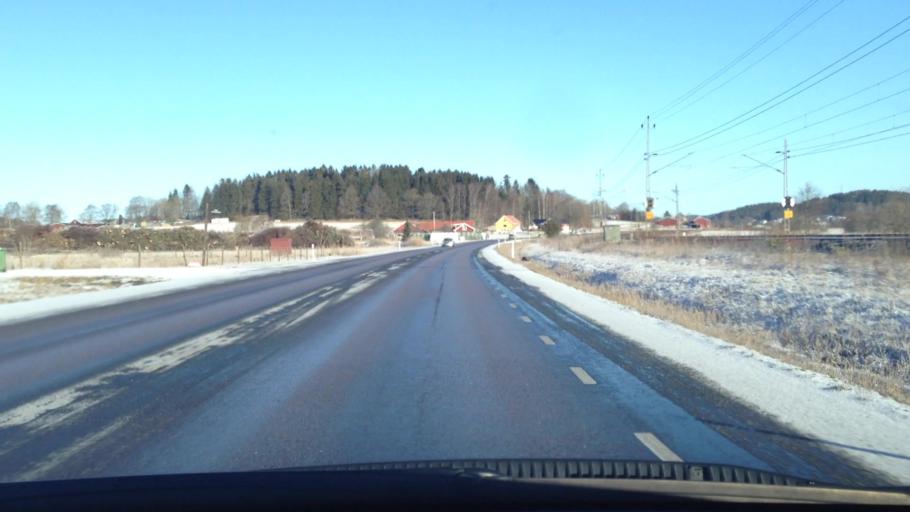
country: SE
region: Vaestra Goetaland
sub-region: Molndal
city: Lindome
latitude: 57.5581
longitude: 12.0855
